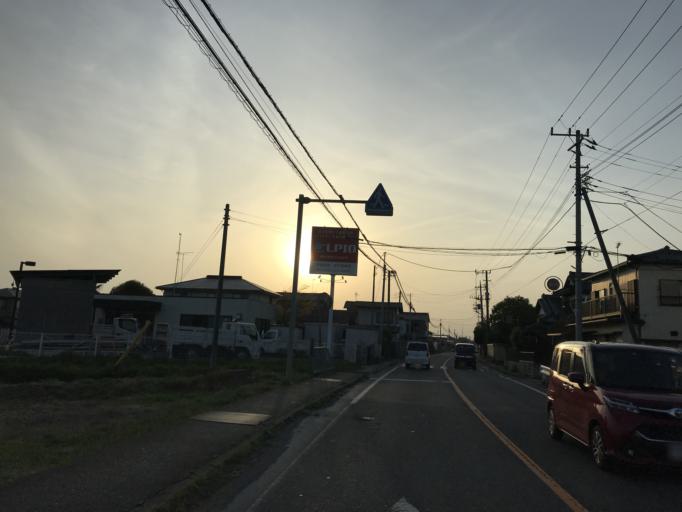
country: JP
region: Ibaraki
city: Katsuta
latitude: 36.3672
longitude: 140.5099
